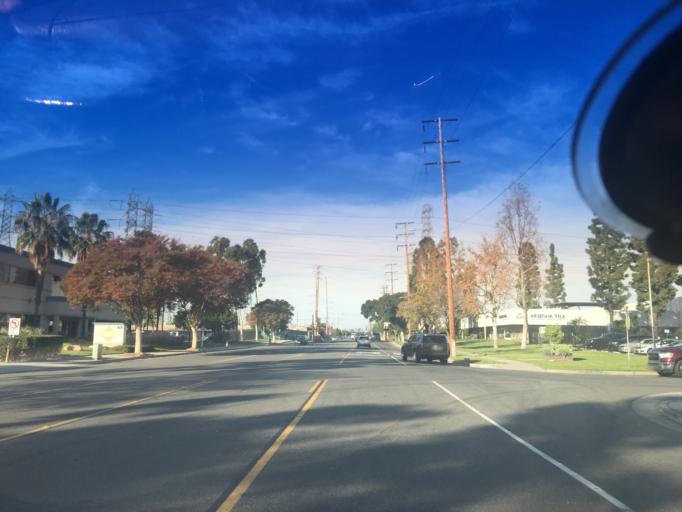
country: US
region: California
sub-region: Orange County
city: Anaheim
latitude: 33.8059
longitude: -117.8977
